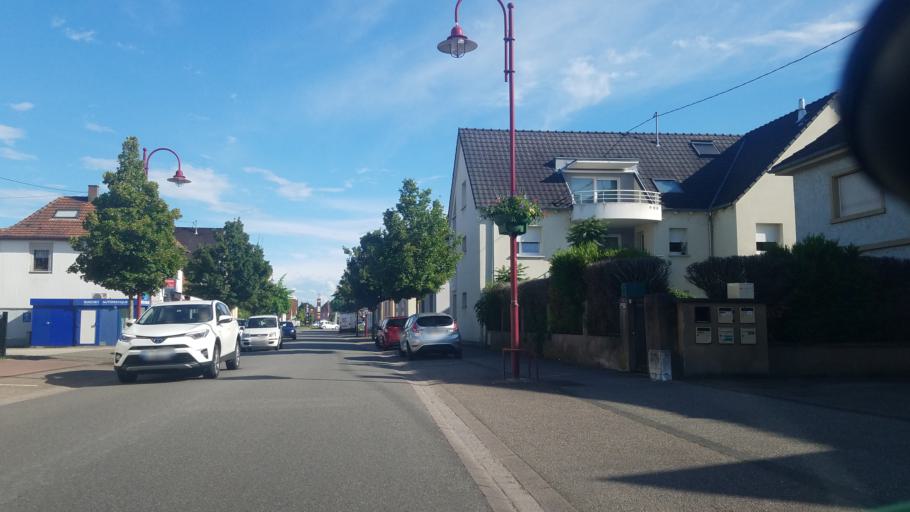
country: FR
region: Alsace
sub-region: Departement du Bas-Rhin
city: Drusenheim
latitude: 48.7605
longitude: 7.9518
